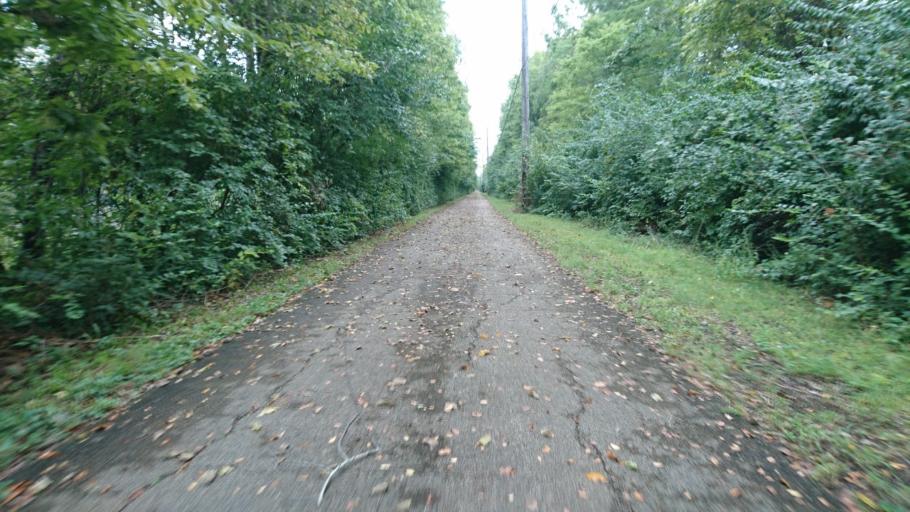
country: US
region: Illinois
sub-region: Sangamon County
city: Southern View
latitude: 39.7381
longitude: -89.6696
